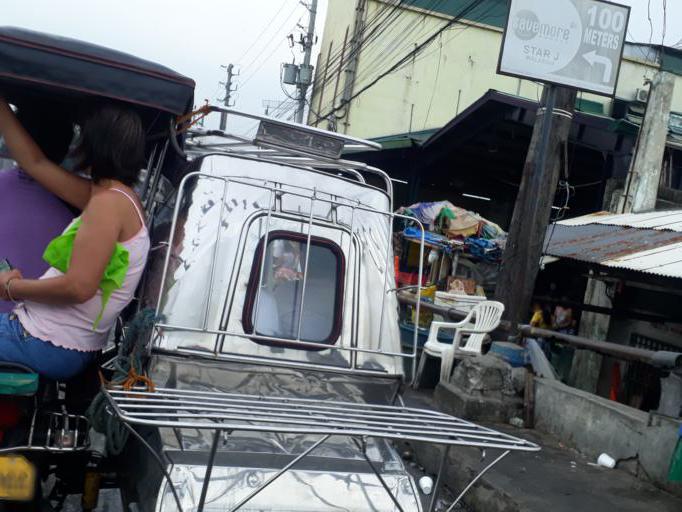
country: PH
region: Metro Manila
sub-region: Caloocan City
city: Niugan
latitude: 14.6556
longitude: 120.9504
